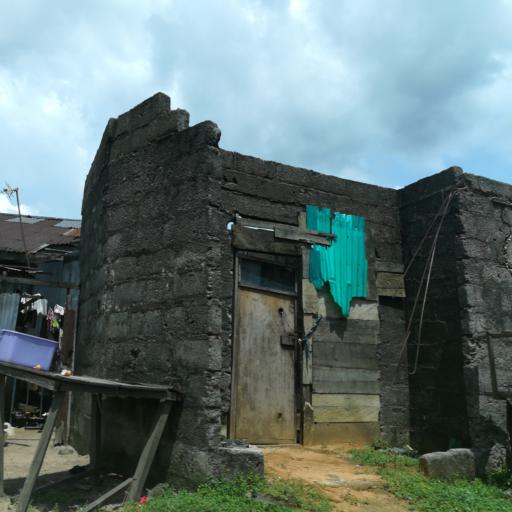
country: NG
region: Rivers
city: Port Harcourt
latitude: 4.7808
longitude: 7.0583
